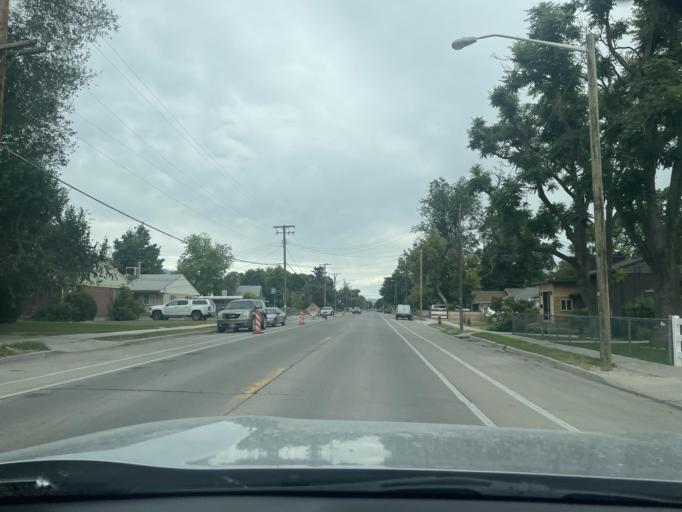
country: US
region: Utah
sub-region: Salt Lake County
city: South Salt Lake
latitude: 40.7088
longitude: -111.8769
